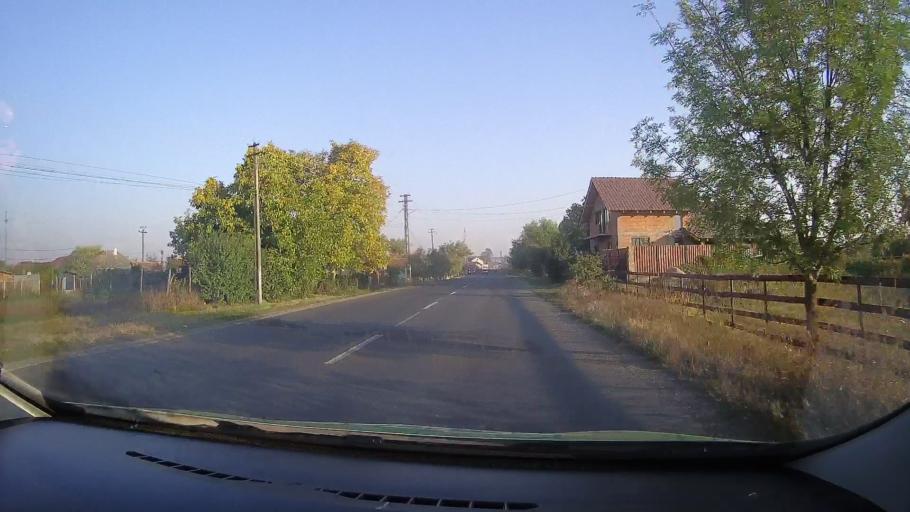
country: RO
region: Arad
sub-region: Comuna Sofronea
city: Sofronea
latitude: 46.2738
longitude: 21.3148
